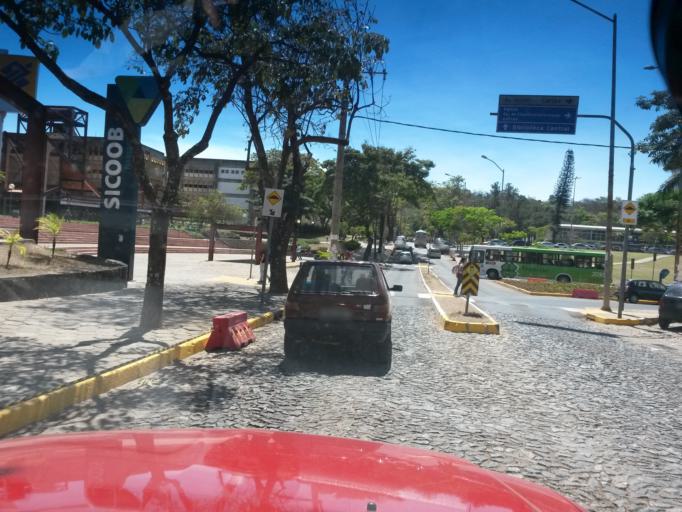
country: BR
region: Minas Gerais
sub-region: Belo Horizonte
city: Belo Horizonte
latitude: -19.8679
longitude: -43.9641
